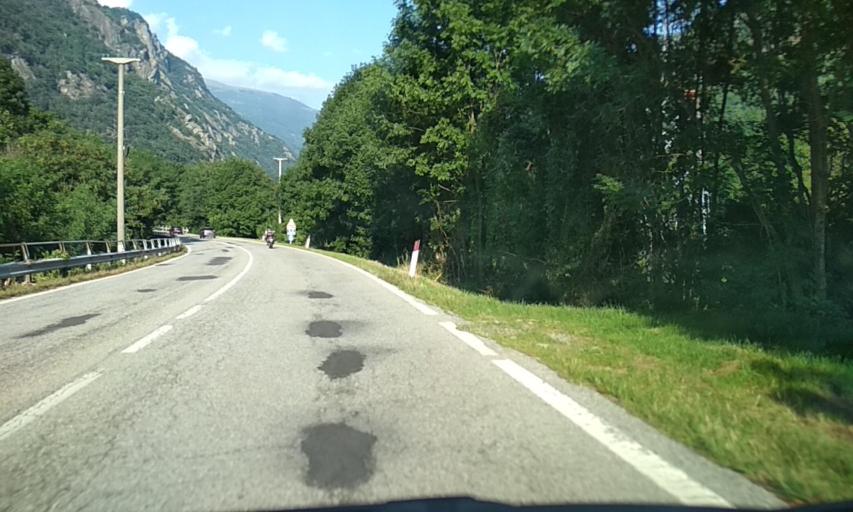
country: IT
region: Piedmont
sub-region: Provincia di Torino
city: Sparone
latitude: 45.4157
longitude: 7.5562
